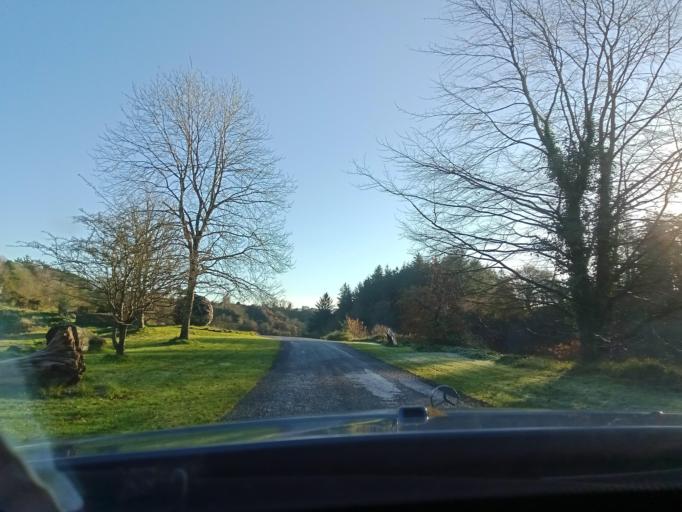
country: IE
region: Munster
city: Carrick-on-Suir
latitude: 52.4258
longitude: -7.3885
